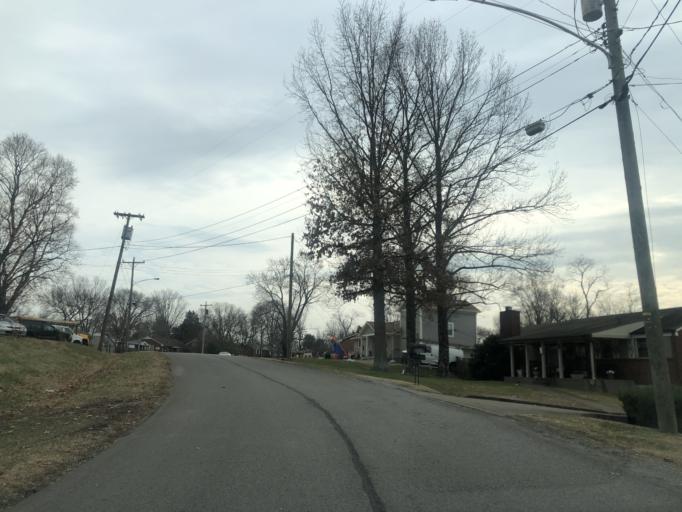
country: US
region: Tennessee
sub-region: Davidson County
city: Oak Hill
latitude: 36.0882
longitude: -86.7197
